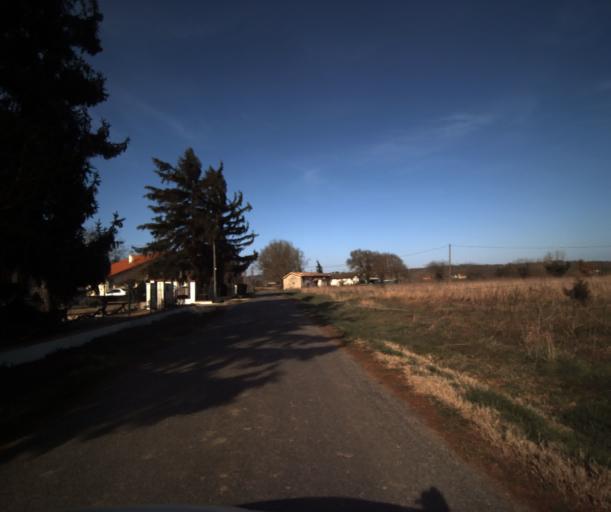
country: FR
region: Midi-Pyrenees
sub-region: Departement du Tarn-et-Garonne
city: Labastide-Saint-Pierre
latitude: 43.9289
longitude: 1.3554
